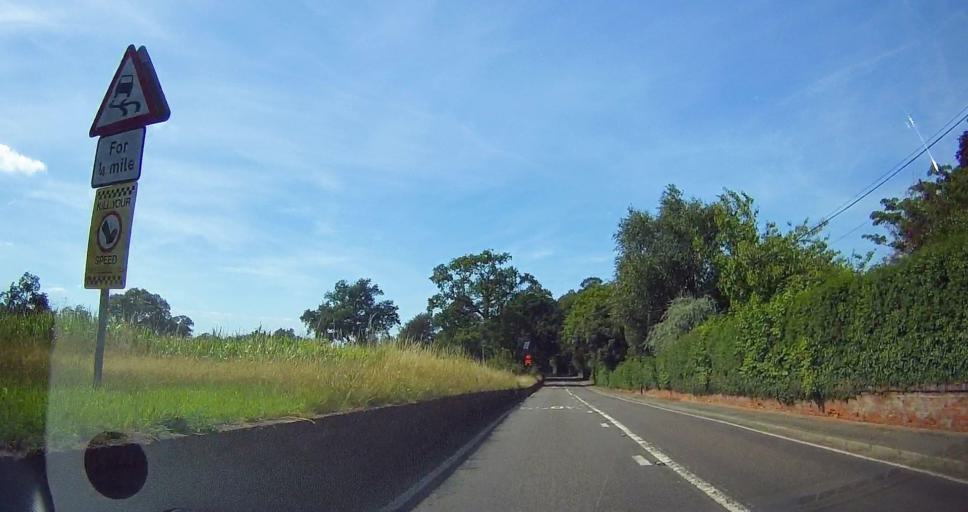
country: GB
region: England
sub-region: Shropshire
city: Market Drayton
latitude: 52.9574
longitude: -2.5057
